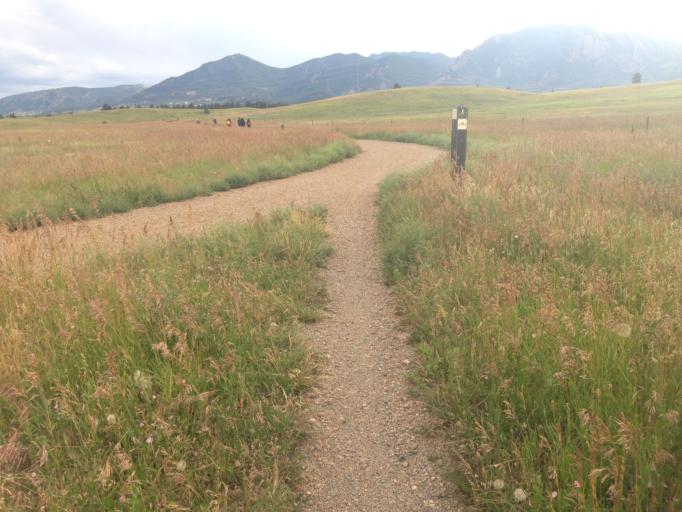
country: US
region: Colorado
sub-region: Boulder County
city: Superior
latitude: 39.9255
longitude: -105.2366
